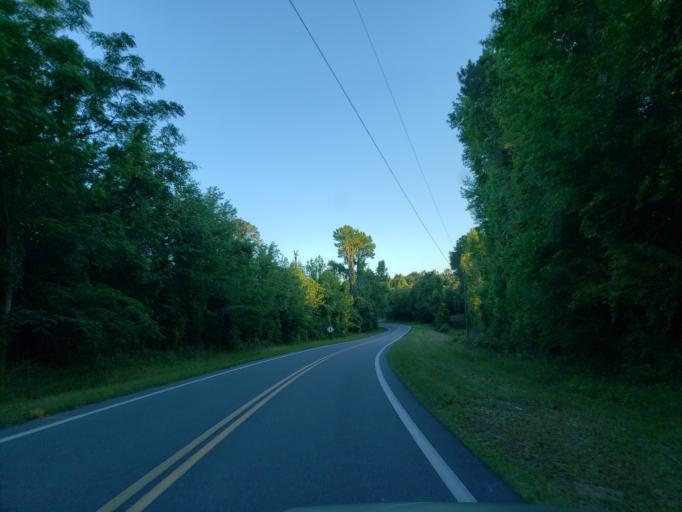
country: US
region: Florida
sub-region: Madison County
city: Madison
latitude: 30.6166
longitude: -83.2552
